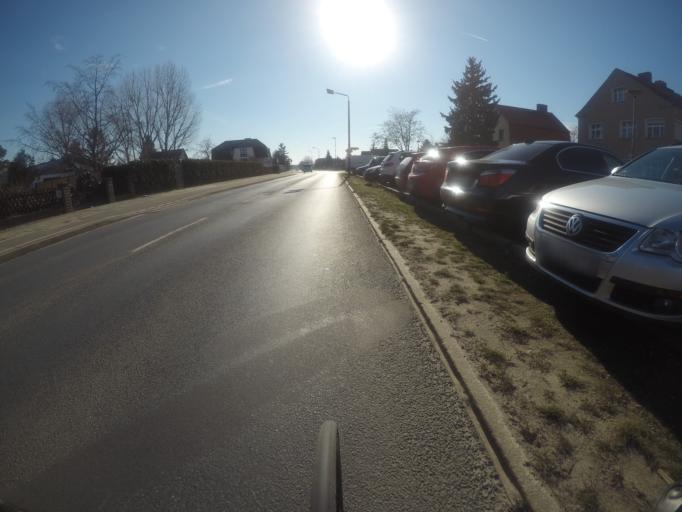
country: DE
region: Berlin
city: Kaulsdorf
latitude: 52.4960
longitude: 13.5771
